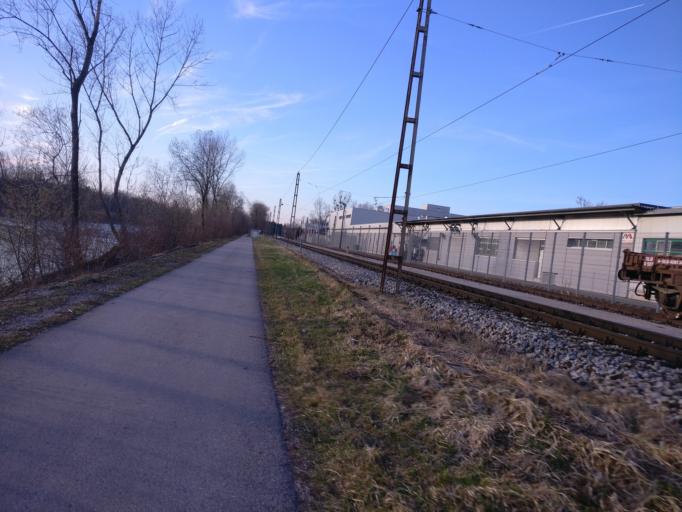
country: AT
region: Salzburg
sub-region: Politischer Bezirk Salzburg-Umgebung
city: Bergheim
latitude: 47.8446
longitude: 13.0141
